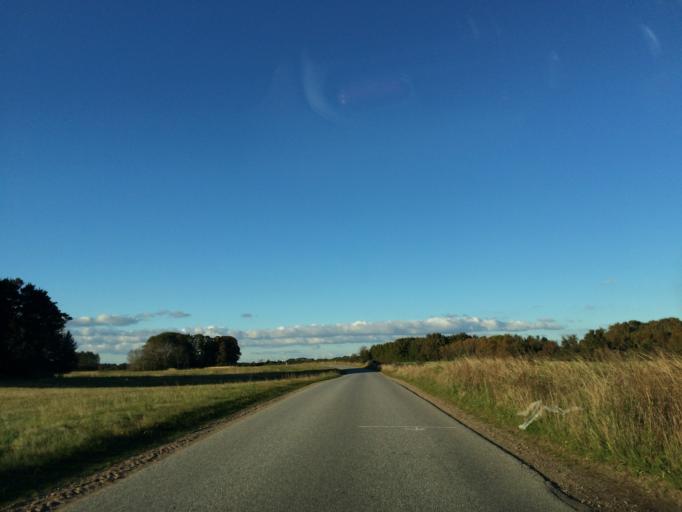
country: DK
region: Central Jutland
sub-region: Silkeborg Kommune
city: Svejbaek
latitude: 56.1754
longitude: 9.6935
